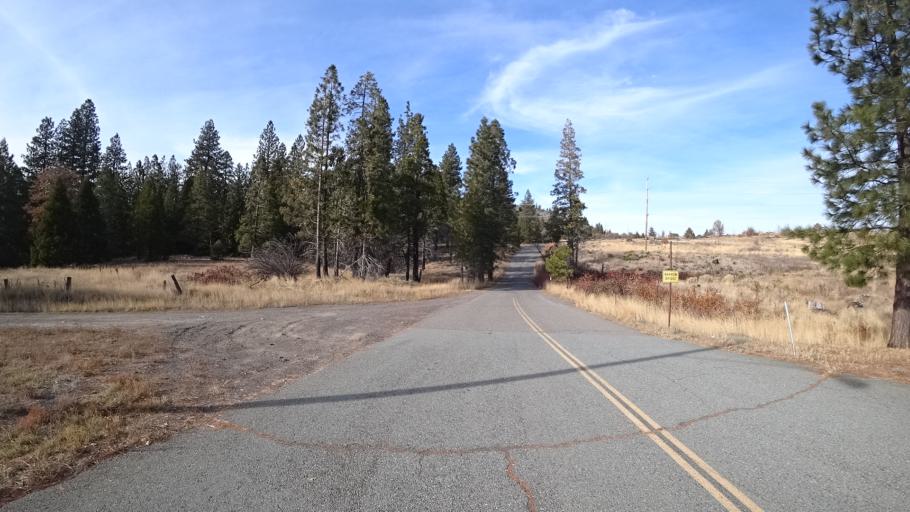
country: US
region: California
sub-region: Siskiyou County
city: Weed
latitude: 41.4405
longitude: -122.3861
